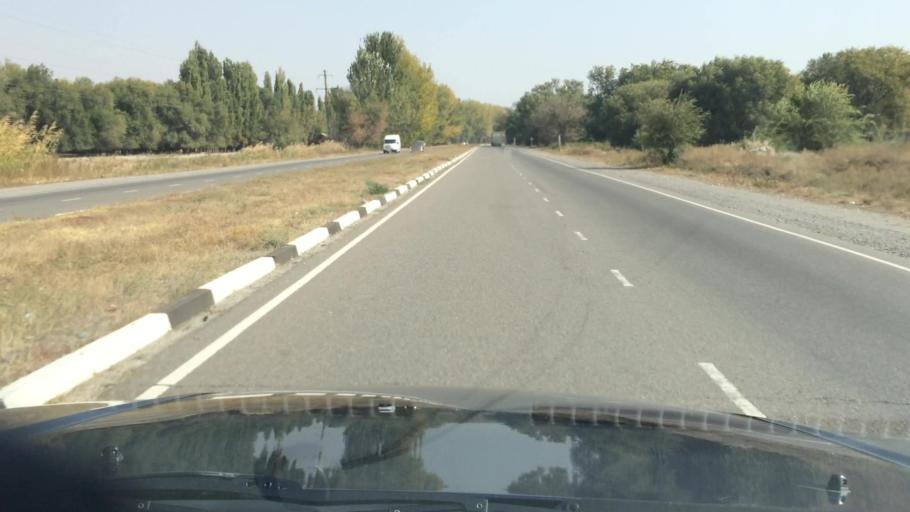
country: KG
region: Chuy
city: Kant
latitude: 42.9714
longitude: 74.8533
